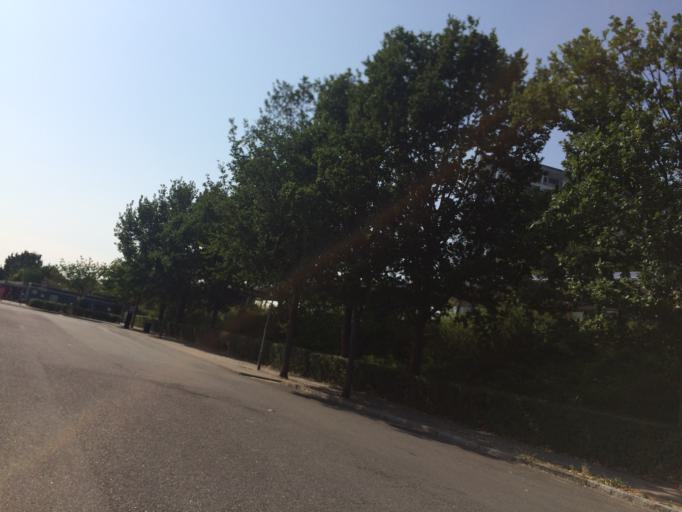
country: DK
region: Capital Region
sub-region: Hvidovre Kommune
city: Hvidovre
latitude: 55.6254
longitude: 12.4558
